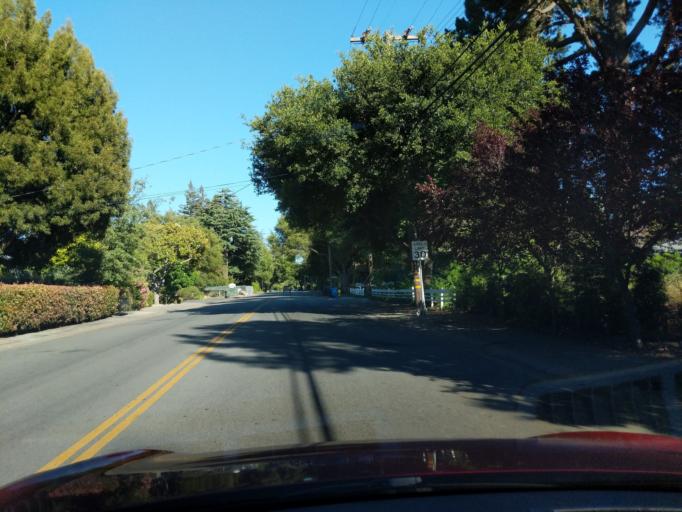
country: US
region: California
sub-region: San Mateo County
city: West Menlo Park
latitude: 37.4401
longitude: -122.1933
